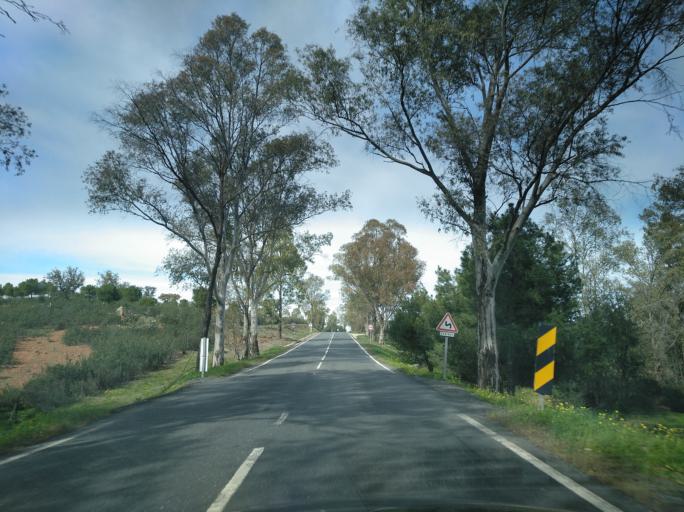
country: PT
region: Beja
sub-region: Mertola
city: Mertola
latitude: 37.7149
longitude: -7.7554
